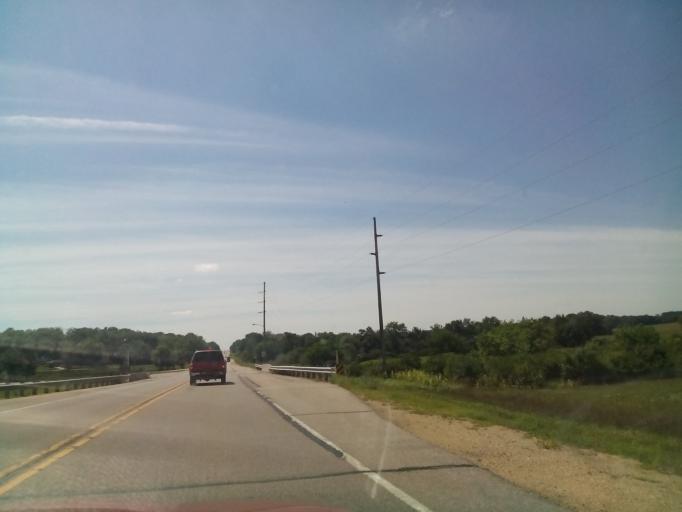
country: US
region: Wisconsin
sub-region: Green County
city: Monticello
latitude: 42.7467
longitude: -89.5994
